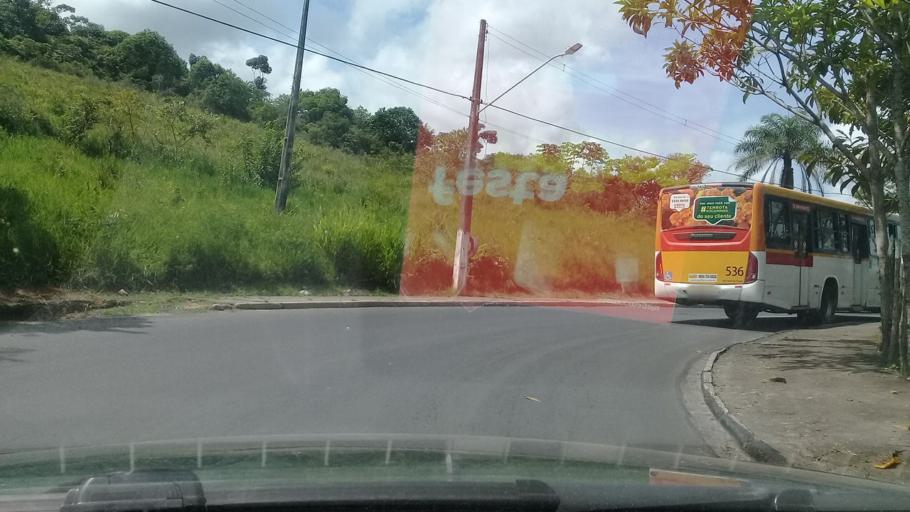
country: BR
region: Pernambuco
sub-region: Jaboatao Dos Guararapes
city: Jaboatao dos Guararapes
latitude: -8.0891
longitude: -35.0238
